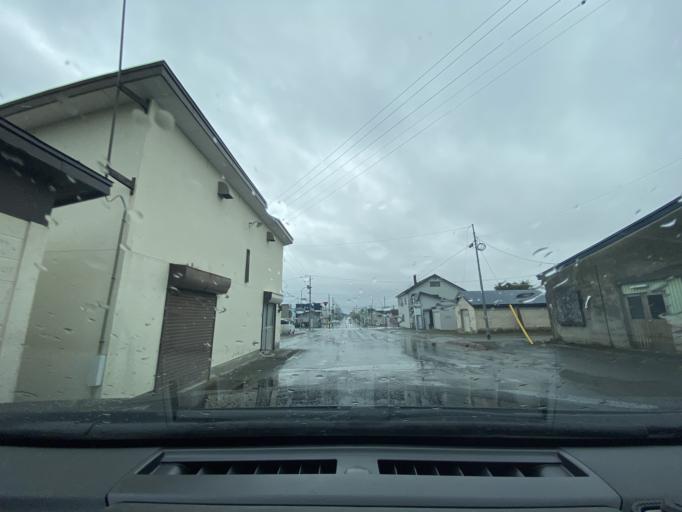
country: JP
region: Hokkaido
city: Fukagawa
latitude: 43.8104
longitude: 141.9322
